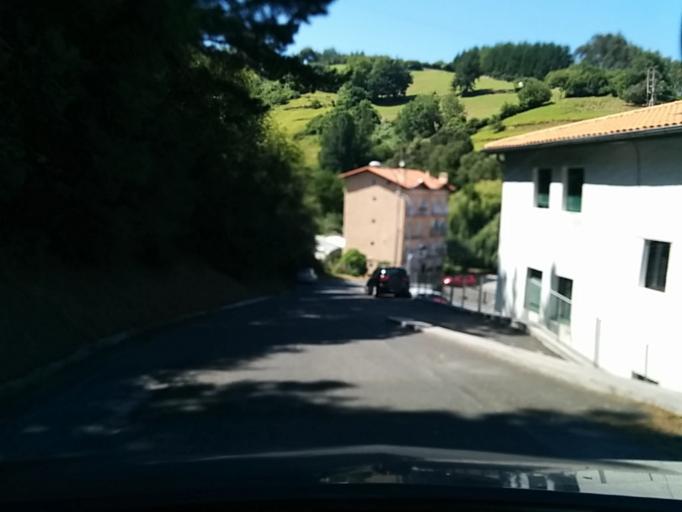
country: ES
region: Basque Country
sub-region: Provincia de Guipuzcoa
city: Zumaia
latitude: 43.2897
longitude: -2.2594
